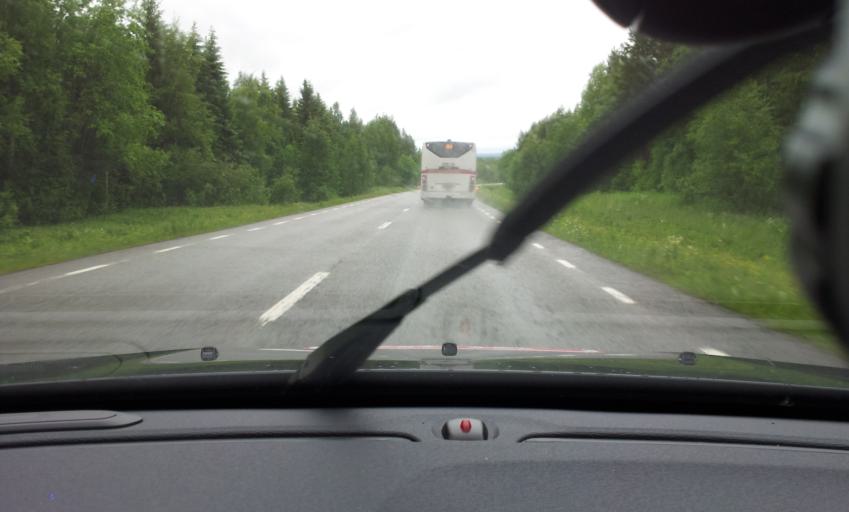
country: SE
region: Jaemtland
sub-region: Krokoms Kommun
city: Krokom
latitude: 63.5894
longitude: 14.6391
